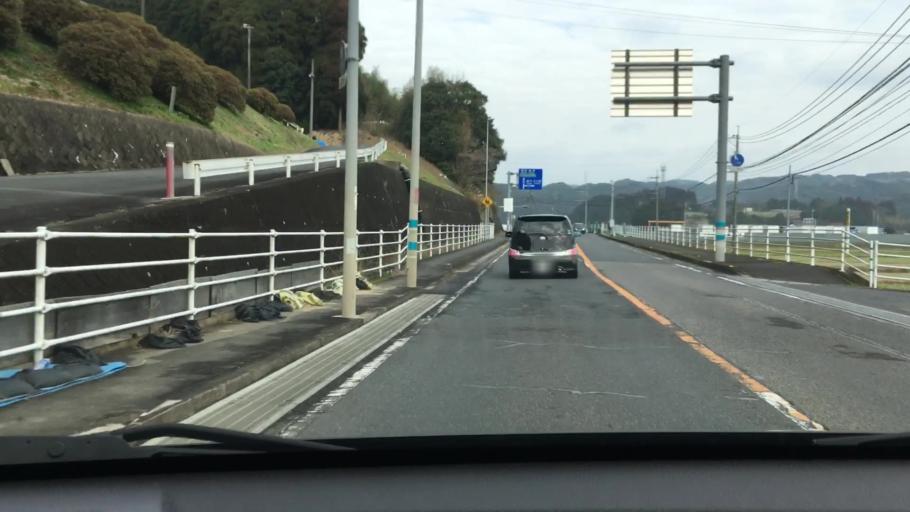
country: JP
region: Saga Prefecture
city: Imaricho-ko
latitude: 33.3054
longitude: 129.9244
